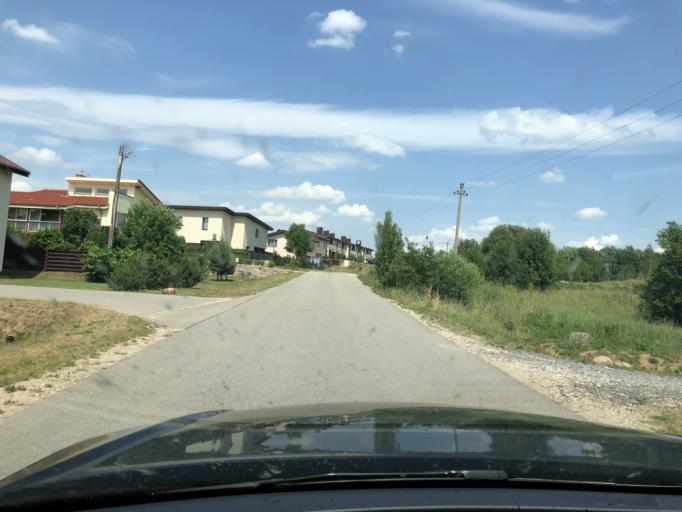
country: LT
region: Vilnius County
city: Pasilaiciai
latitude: 54.7506
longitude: 25.1909
